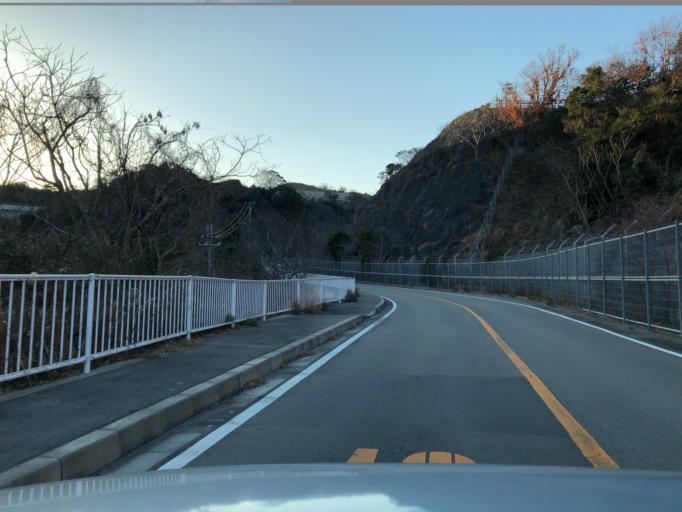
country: JP
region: Wakayama
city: Tanabe
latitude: 33.6629
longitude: 135.3709
